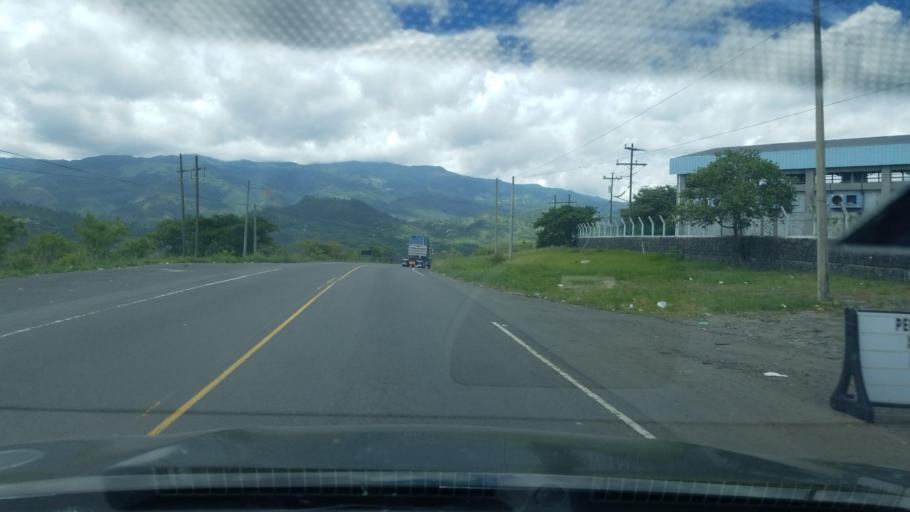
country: HN
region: Francisco Morazan
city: Cofradia
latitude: 14.2060
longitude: -87.2124
